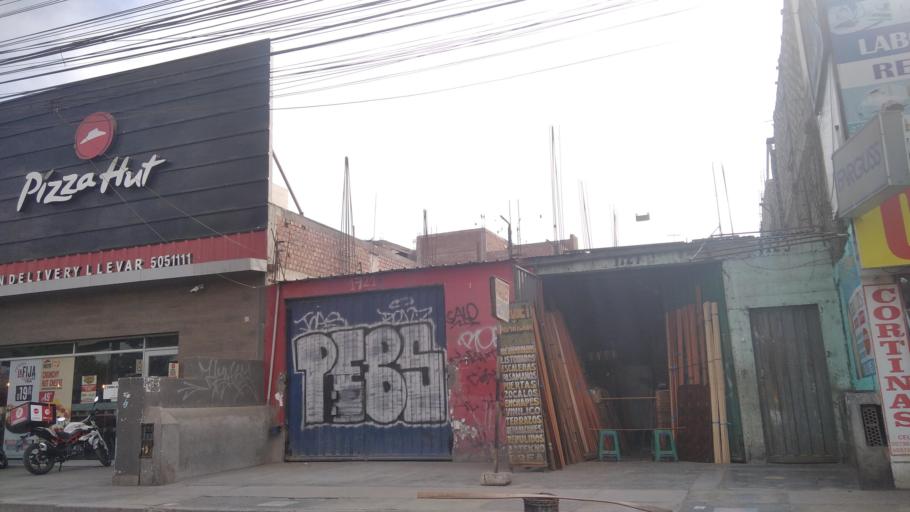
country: PE
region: Lima
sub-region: Lima
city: Independencia
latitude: -12.0053
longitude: -77.0068
